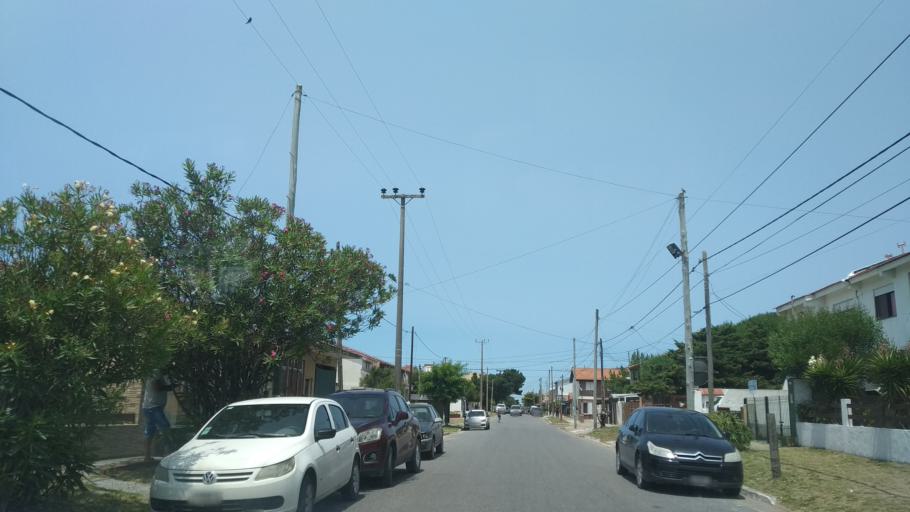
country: AR
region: Buenos Aires
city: Mar del Tuyu
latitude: -36.5572
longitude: -56.6896
